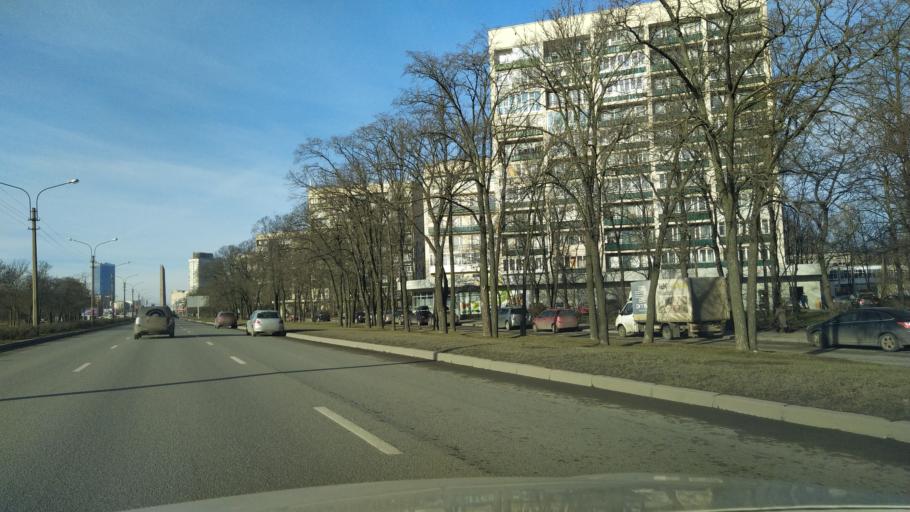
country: RU
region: St.-Petersburg
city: Kupchino
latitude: 59.8383
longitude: 30.3307
